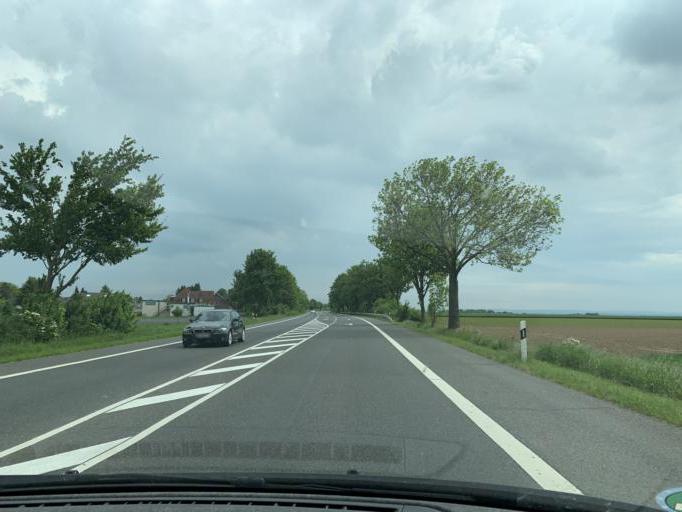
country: DE
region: North Rhine-Westphalia
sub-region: Regierungsbezirk Koln
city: Norvenich
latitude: 50.7899
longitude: 6.6351
